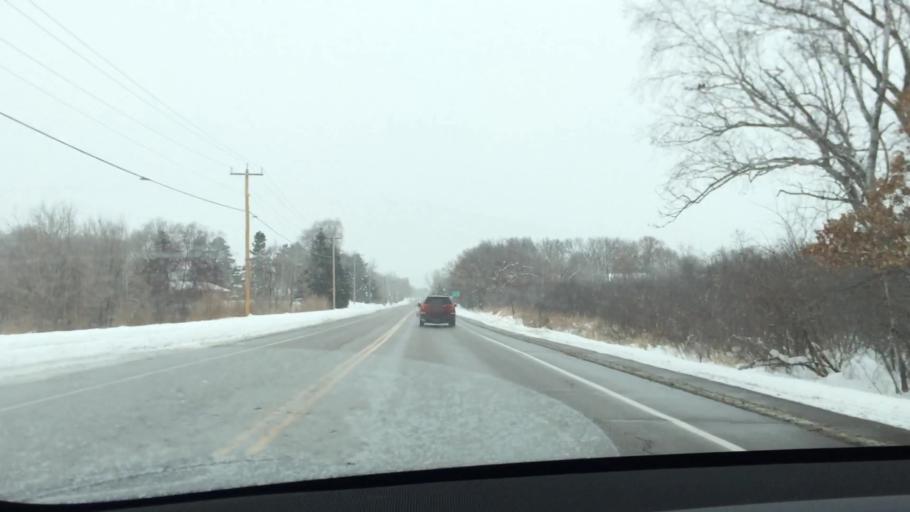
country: US
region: Minnesota
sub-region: Ramsey County
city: Shoreview
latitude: 45.1127
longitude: -93.1274
